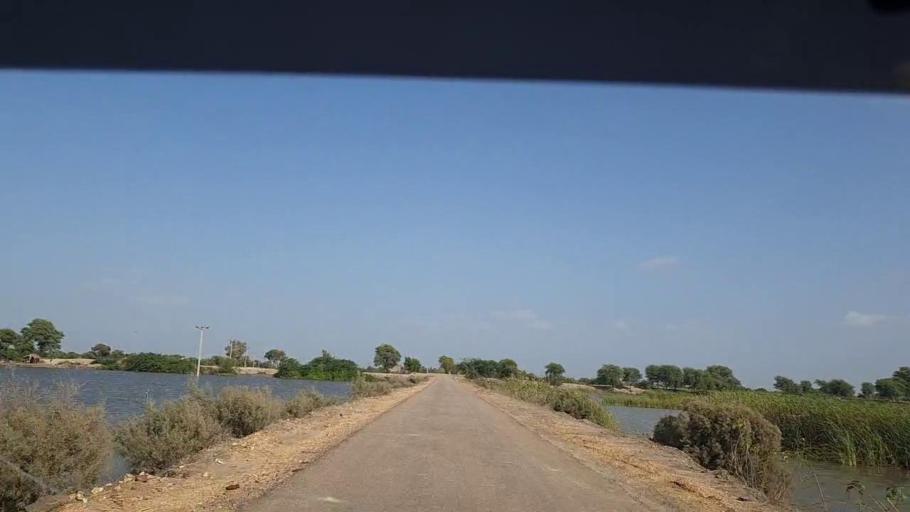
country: PK
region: Sindh
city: Kadhan
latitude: 24.4640
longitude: 68.8451
